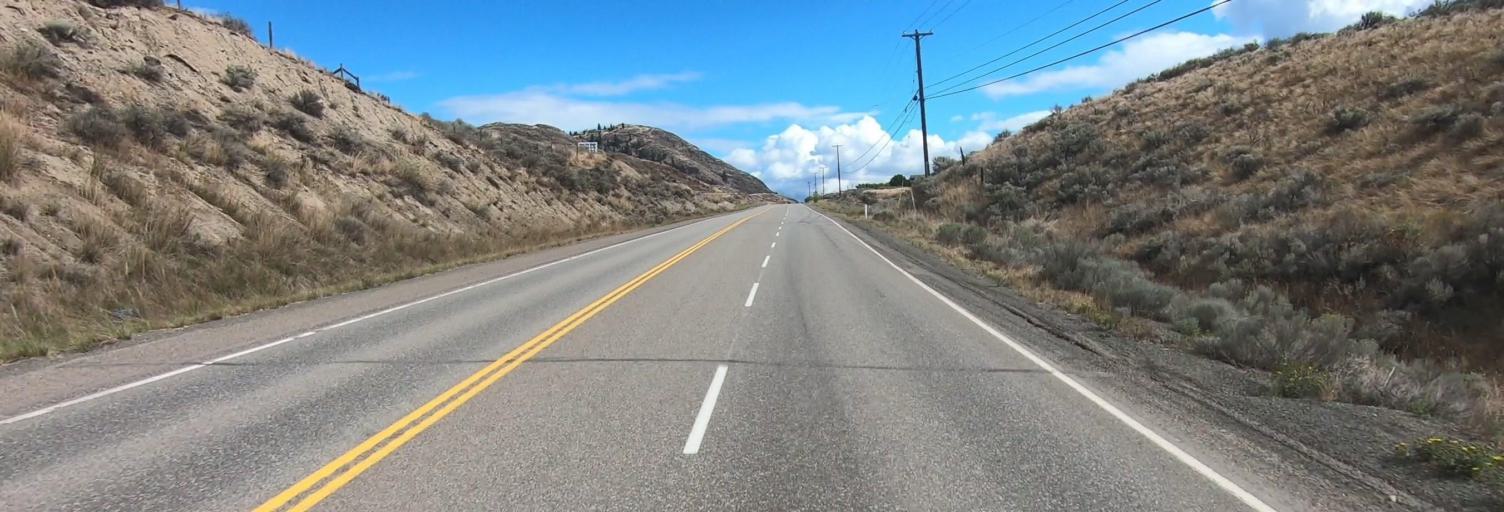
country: CA
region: British Columbia
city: Logan Lake
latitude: 50.7168
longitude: -120.6330
